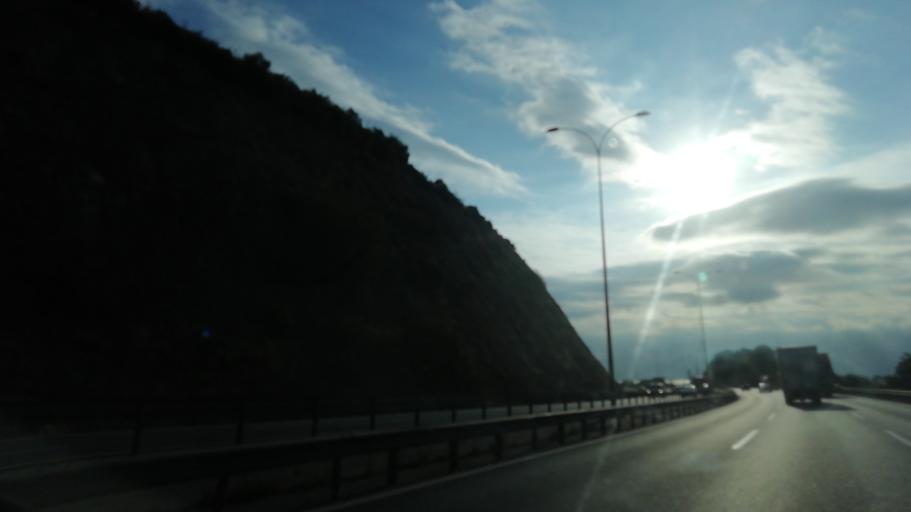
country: TR
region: Kocaeli
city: Hereke
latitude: 40.7795
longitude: 29.6299
